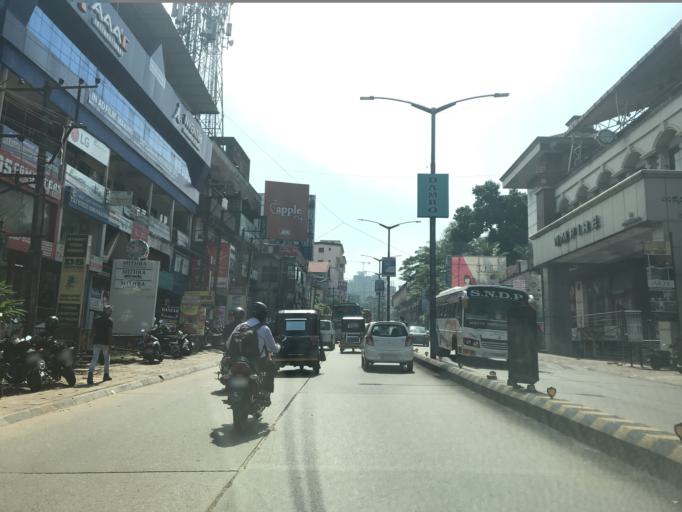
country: IN
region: Karnataka
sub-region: Dakshina Kannada
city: Mangalore
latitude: 12.8802
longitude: 74.8405
